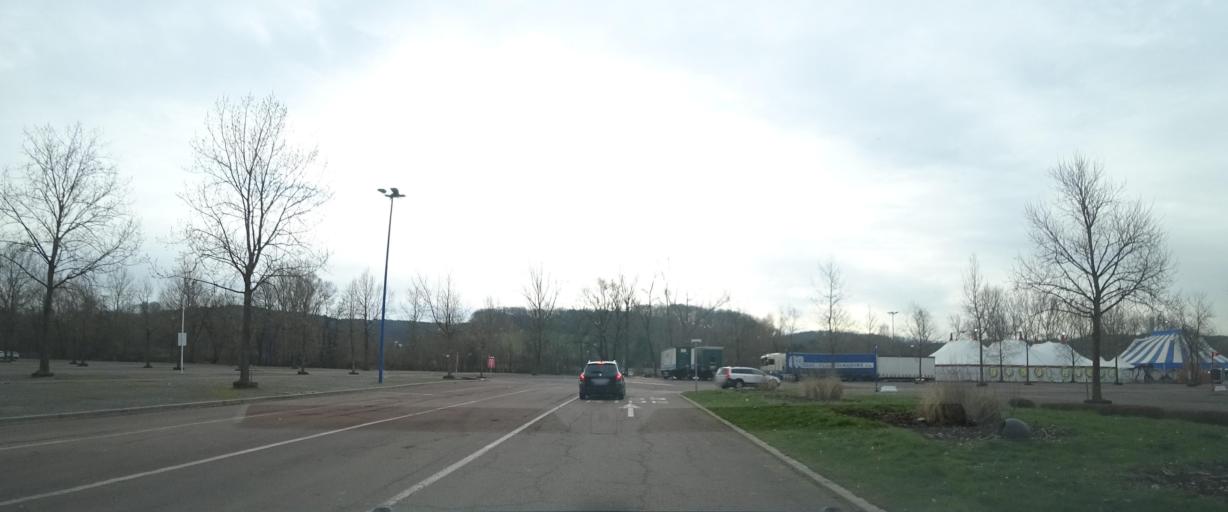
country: BE
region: Wallonia
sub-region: Province du Brabant Wallon
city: Wavre
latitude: 50.7036
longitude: 4.5962
